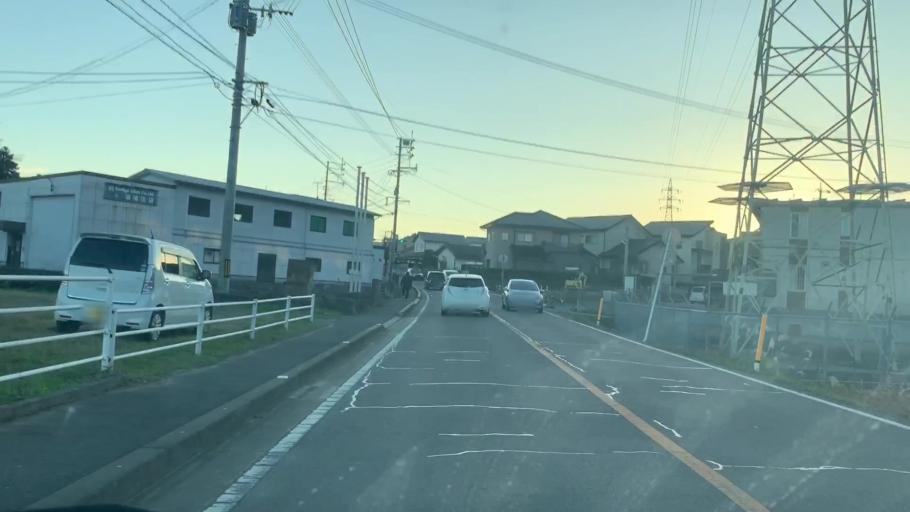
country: JP
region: Saga Prefecture
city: Takeocho-takeo
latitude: 33.2083
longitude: 130.0275
